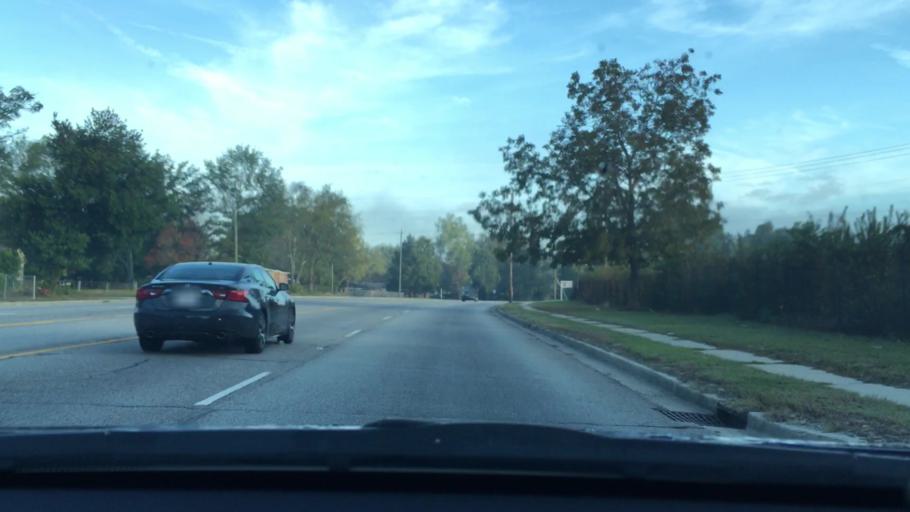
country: US
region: South Carolina
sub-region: Sumter County
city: South Sumter
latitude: 33.9012
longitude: -80.3371
